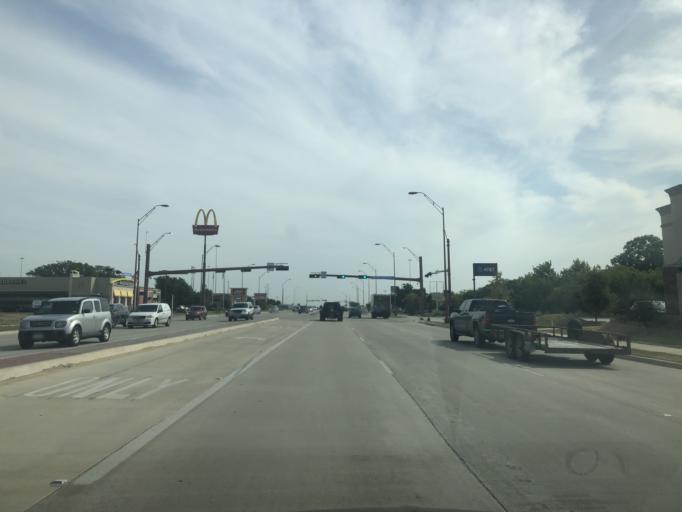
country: US
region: Texas
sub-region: Tarrant County
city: Benbrook
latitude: 32.6803
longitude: -97.4629
